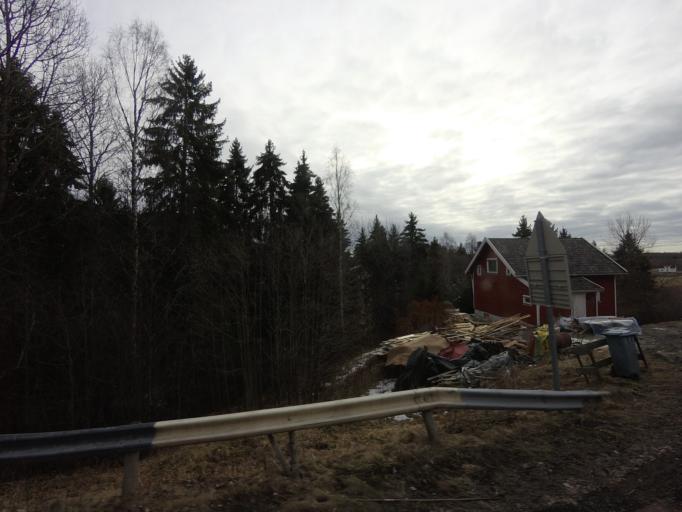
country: NO
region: Akershus
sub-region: Fet
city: Fetsund
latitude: 59.8852
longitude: 11.2105
